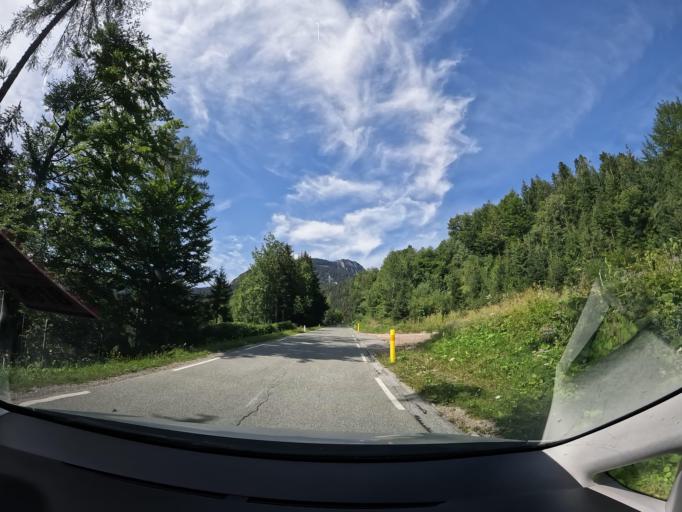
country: AT
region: Carinthia
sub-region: Politischer Bezirk Sankt Veit an der Glan
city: Liebenfels
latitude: 46.7181
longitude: 14.2532
